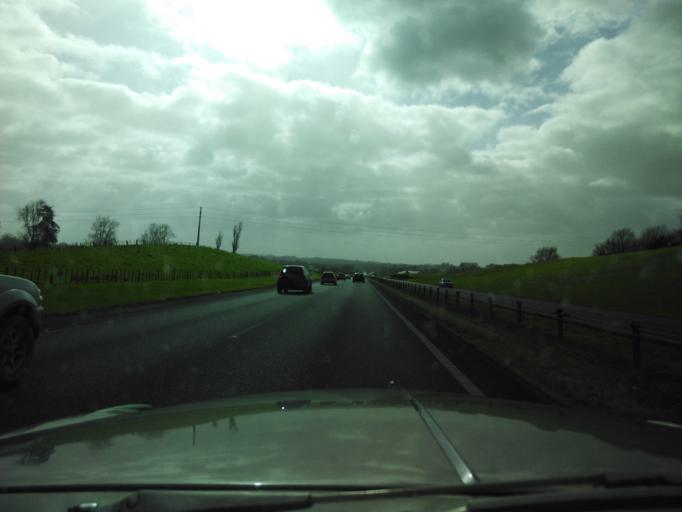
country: NZ
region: Auckland
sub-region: Auckland
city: Rothesay Bay
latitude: -36.6431
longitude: 174.6626
